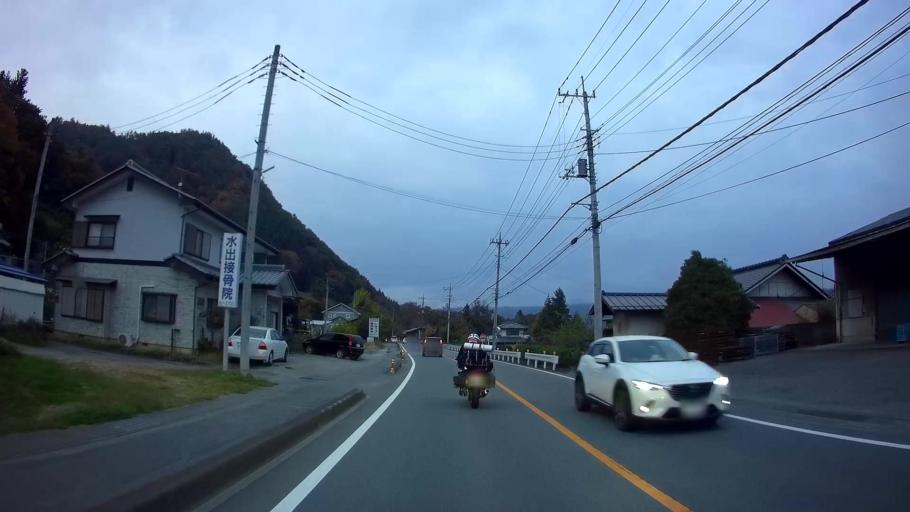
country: JP
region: Gunma
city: Nakanojomachi
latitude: 36.5553
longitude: 138.7754
